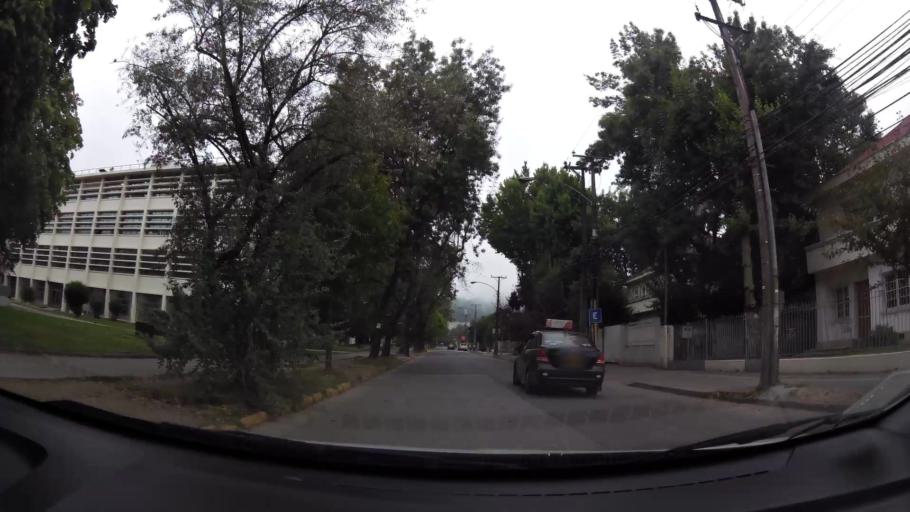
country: CL
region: Biobio
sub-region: Provincia de Concepcion
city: Concepcion
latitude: -36.8299
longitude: -73.0381
